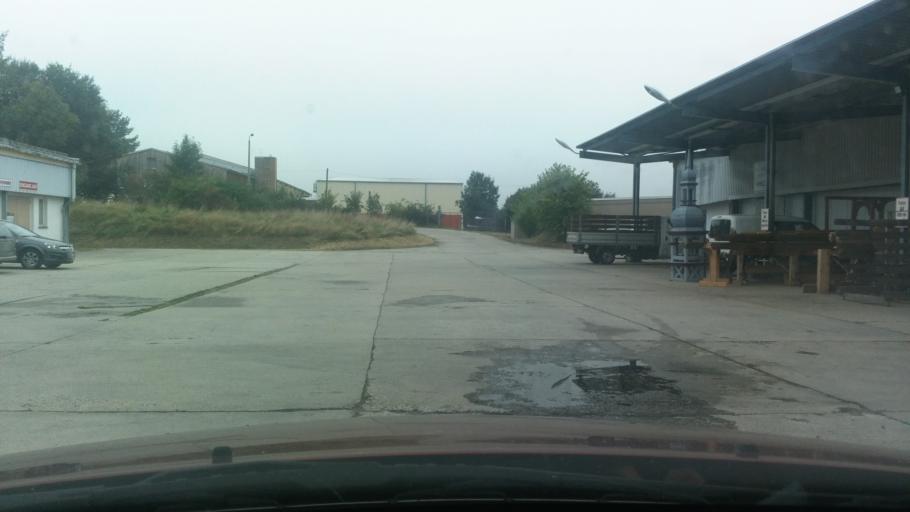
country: DE
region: Saxony
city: Goerlitz
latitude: 51.1230
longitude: 14.9426
